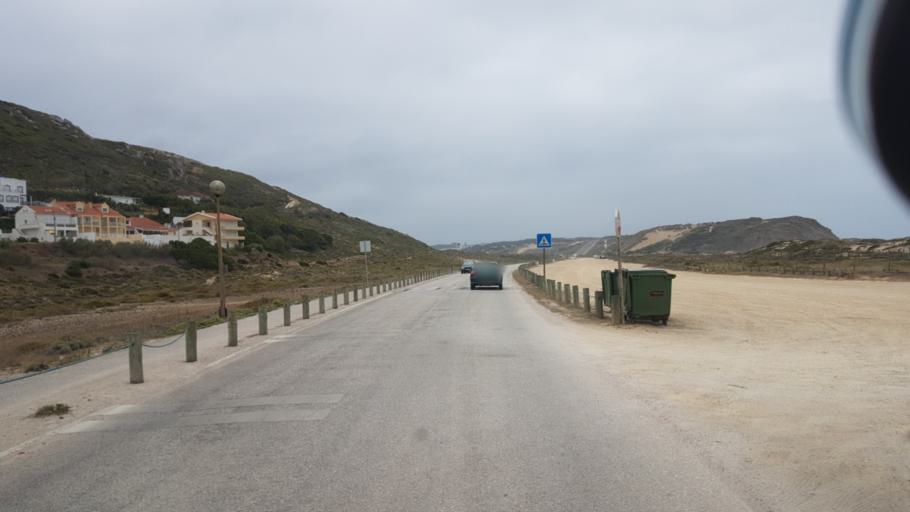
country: PT
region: Lisbon
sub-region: Torres Vedras
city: A dos Cunhados
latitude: 39.1741
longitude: -9.3561
